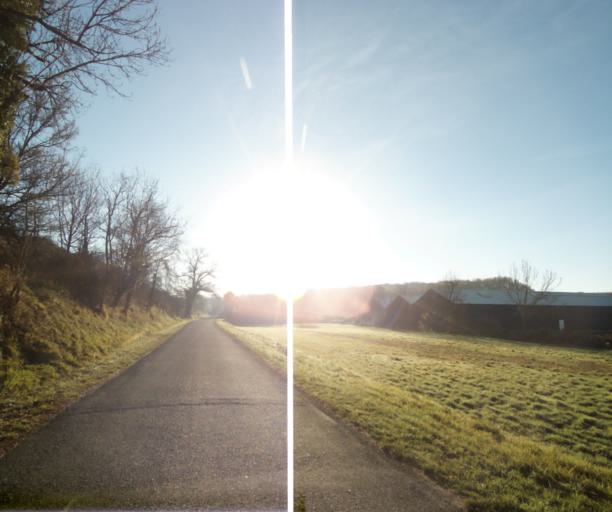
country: FR
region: Poitou-Charentes
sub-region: Departement de la Charente-Maritime
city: Cherac
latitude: 45.7047
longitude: -0.4319
